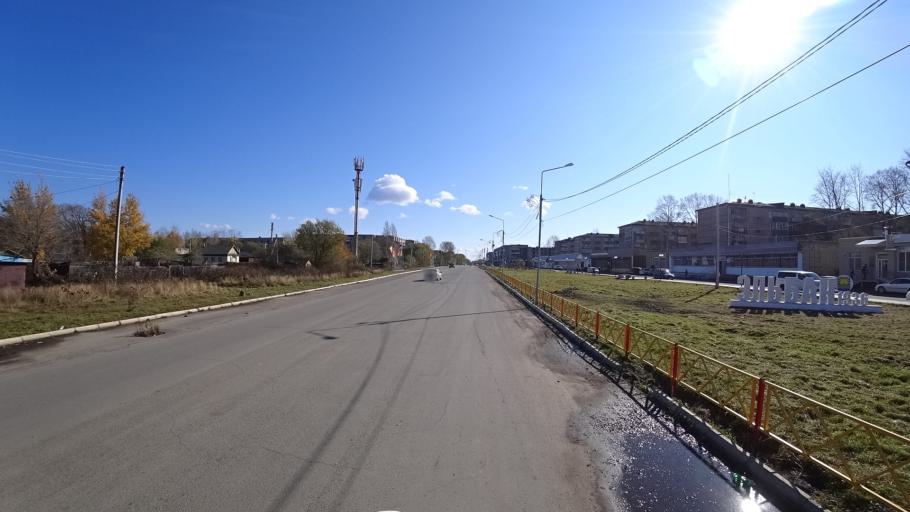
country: RU
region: Khabarovsk Krai
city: Amursk
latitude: 50.1011
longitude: 136.5103
